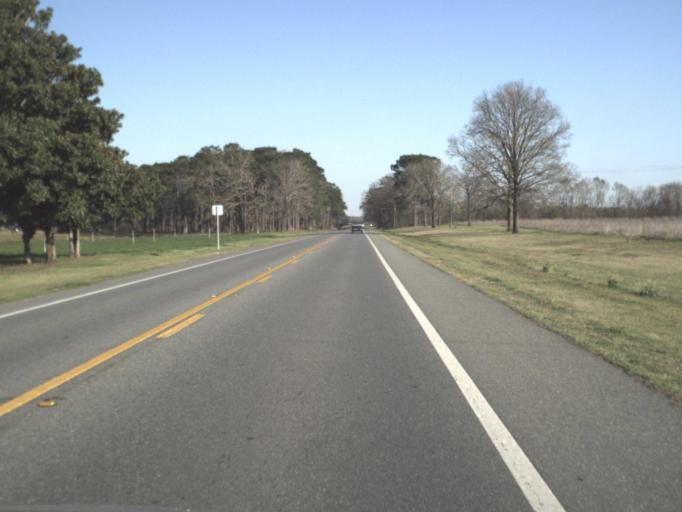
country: US
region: Florida
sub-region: Jackson County
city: Sneads
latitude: 30.7074
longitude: -84.8946
